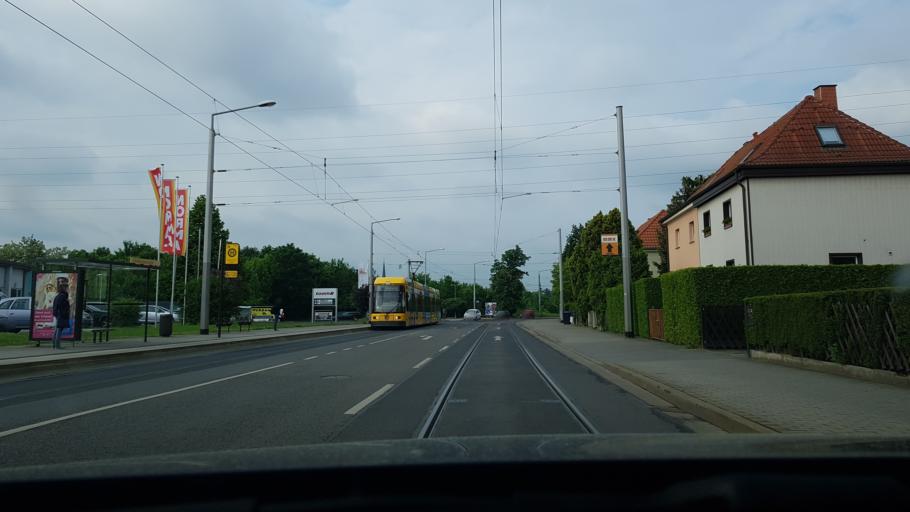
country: DE
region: Saxony
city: Heidenau
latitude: 51.0184
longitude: 13.8314
